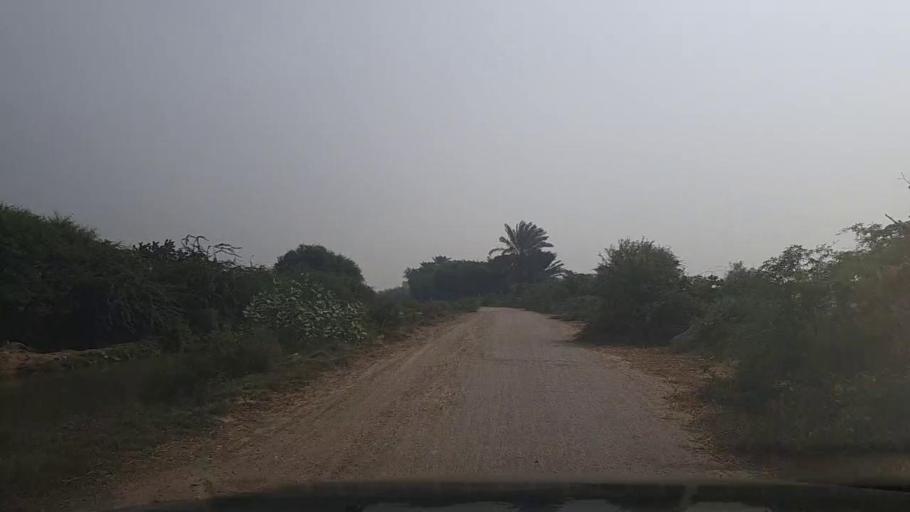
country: PK
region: Sindh
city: Mirpur Sakro
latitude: 24.4808
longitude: 67.6456
